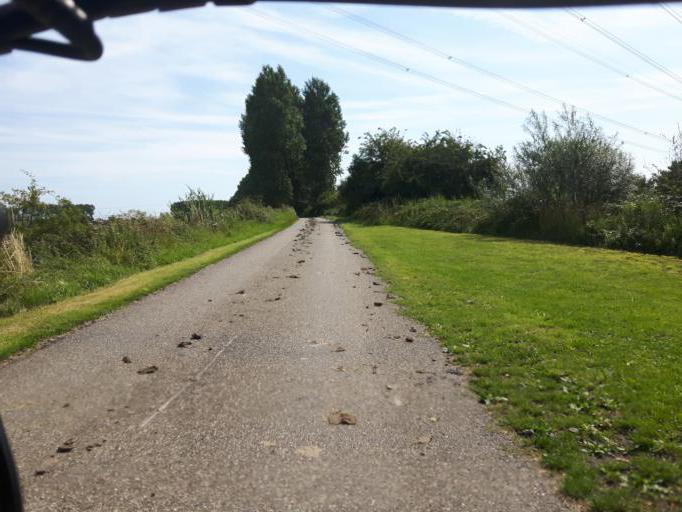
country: NL
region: Zeeland
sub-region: Gemeente Borsele
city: Borssele
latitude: 51.4275
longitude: 3.8033
